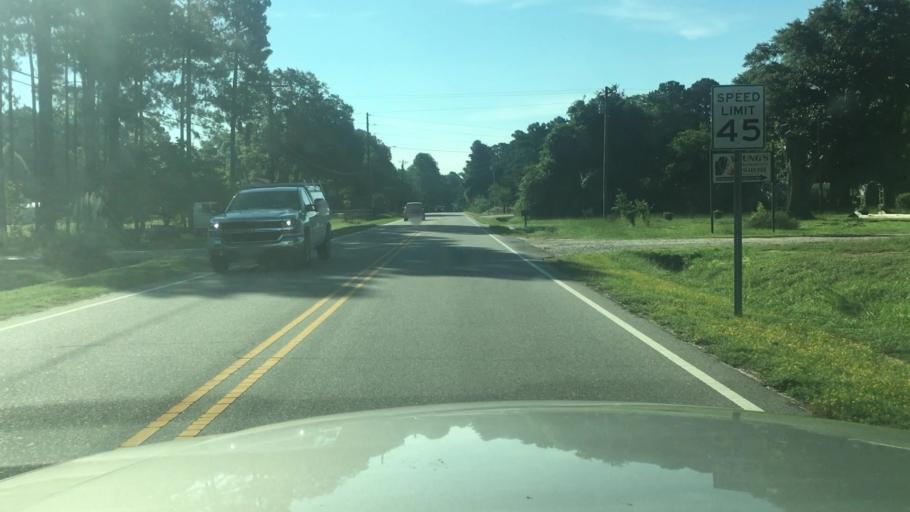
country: US
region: North Carolina
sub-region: Cumberland County
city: Fayetteville
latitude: 35.1283
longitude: -78.8933
